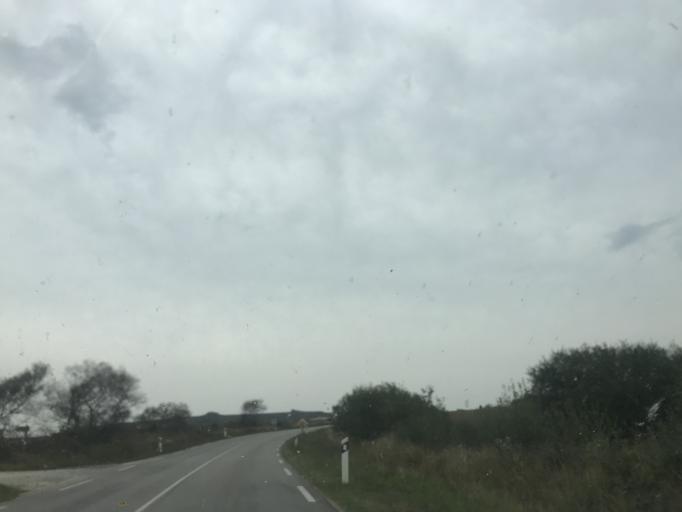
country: FR
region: Brittany
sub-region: Departement du Finistere
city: Brasparts
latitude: 48.3830
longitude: -3.9435
